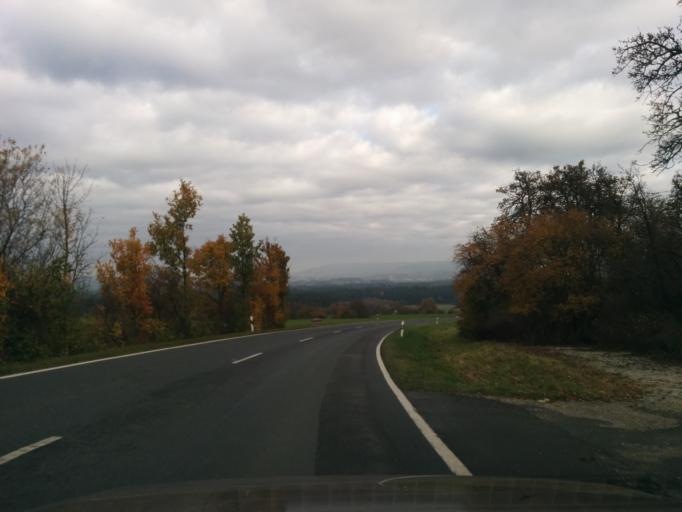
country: DE
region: Bavaria
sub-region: Regierungsbezirk Mittelfranken
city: Kalchreuth
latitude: 49.5607
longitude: 11.1233
